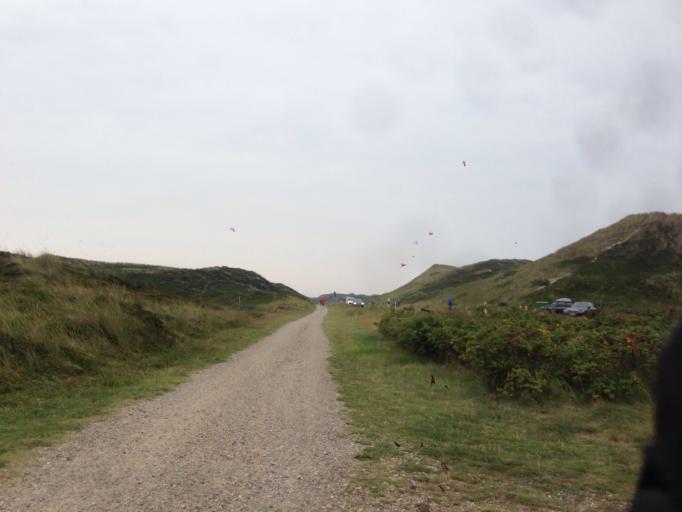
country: DE
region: Schleswig-Holstein
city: Westerland
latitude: 54.8150
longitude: 8.2911
